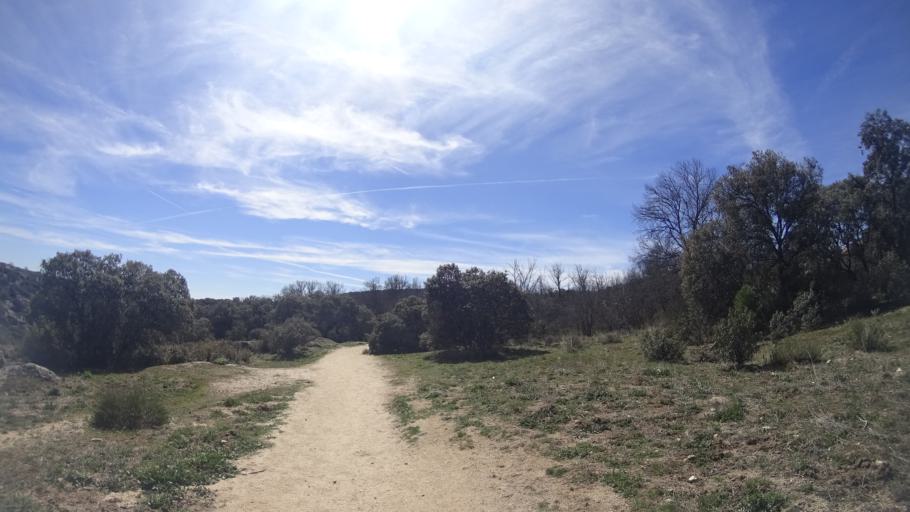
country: ES
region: Madrid
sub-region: Provincia de Madrid
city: Galapagar
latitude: 40.5938
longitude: -3.9774
